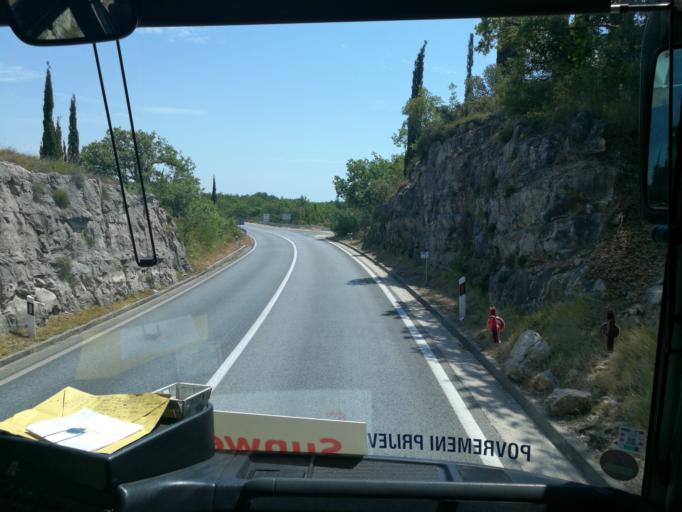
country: HR
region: Dubrovacko-Neretvanska
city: Cavtat
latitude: 42.5651
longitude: 18.2458
